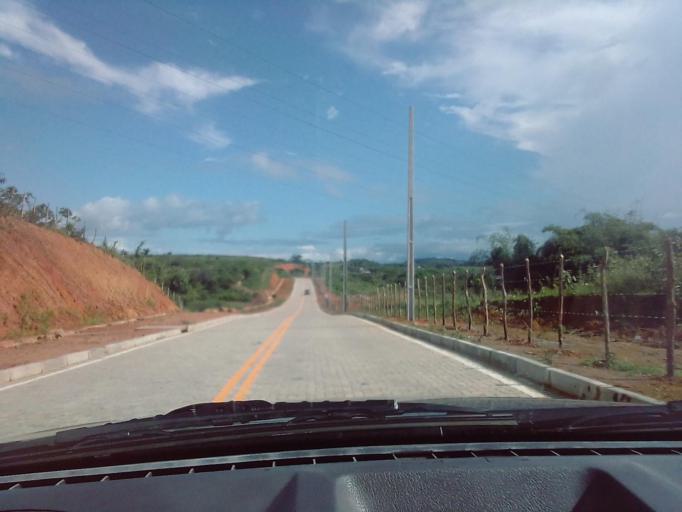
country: BR
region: Pernambuco
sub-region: Jaboatao Dos Guararapes
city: Jaboatao dos Guararapes
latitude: -8.1028
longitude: -35.0334
